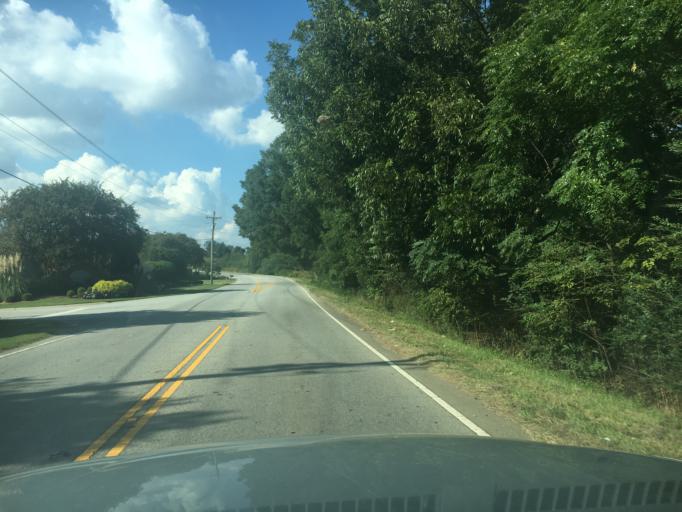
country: US
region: South Carolina
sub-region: Greenville County
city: Simpsonville
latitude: 34.6928
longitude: -82.2529
